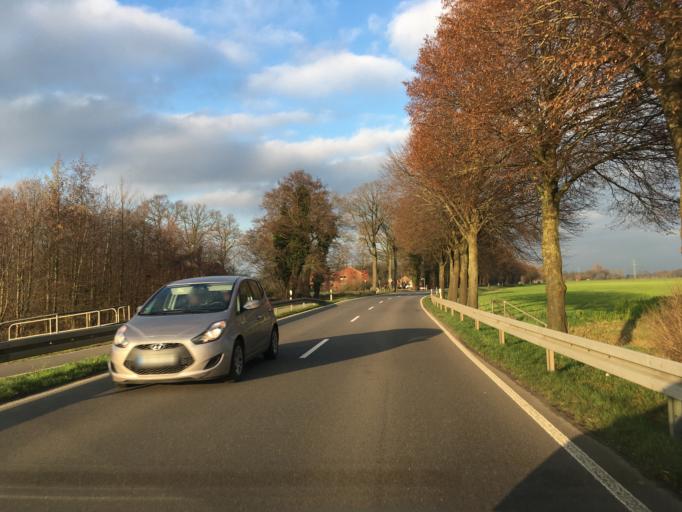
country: DE
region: North Rhine-Westphalia
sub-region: Regierungsbezirk Munster
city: Ahaus
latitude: 52.1356
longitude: 7.0068
